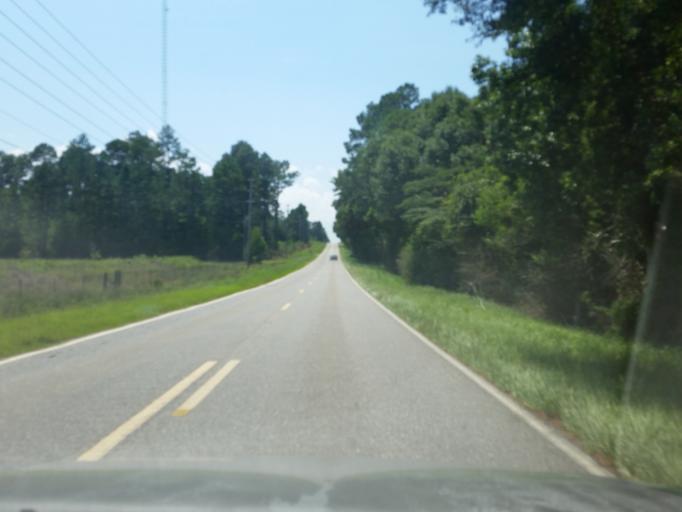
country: US
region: Alabama
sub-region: Baldwin County
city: Robertsdale
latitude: 30.6261
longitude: -87.6434
